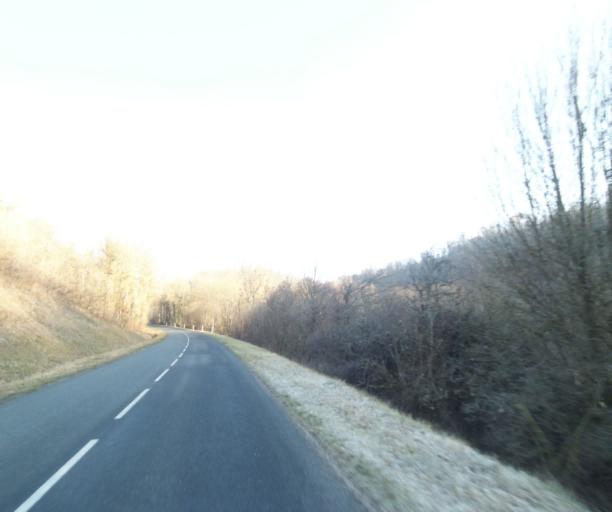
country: FR
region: Champagne-Ardenne
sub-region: Departement de la Haute-Marne
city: Chevillon
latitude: 48.5253
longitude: 5.1607
